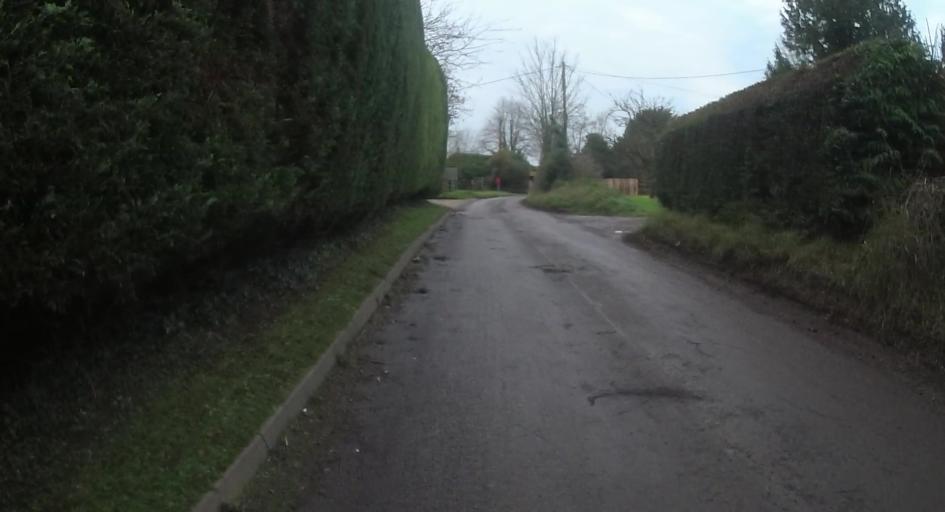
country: GB
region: England
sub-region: Hampshire
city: Basingstoke
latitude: 51.2820
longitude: -1.1573
